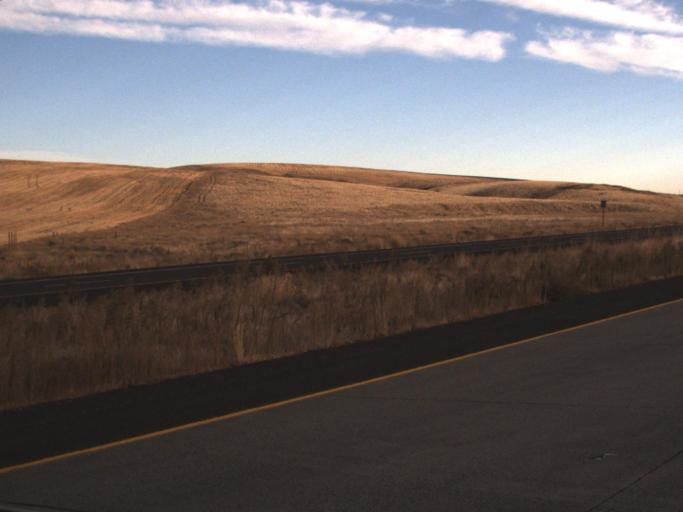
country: US
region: Washington
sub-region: Franklin County
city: Connell
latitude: 46.8371
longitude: -118.6501
